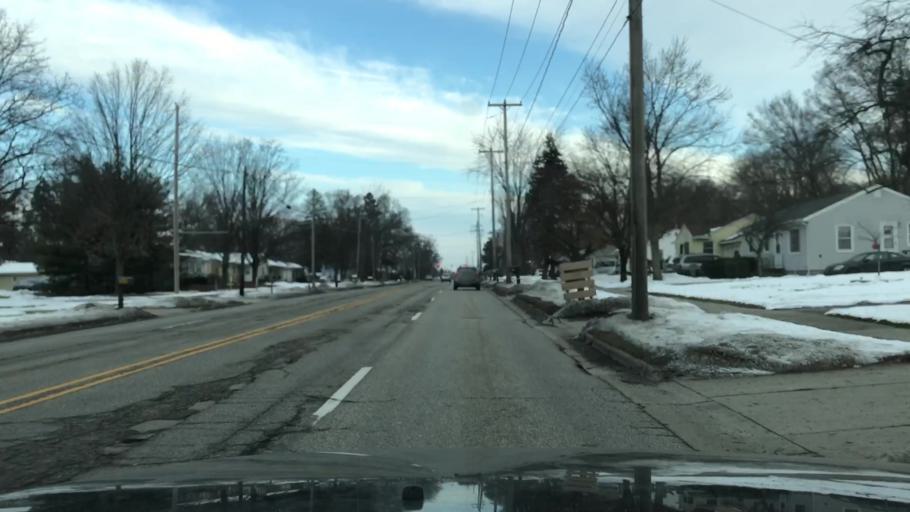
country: US
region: Michigan
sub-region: Kent County
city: Grandville
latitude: 42.9035
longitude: -85.7438
